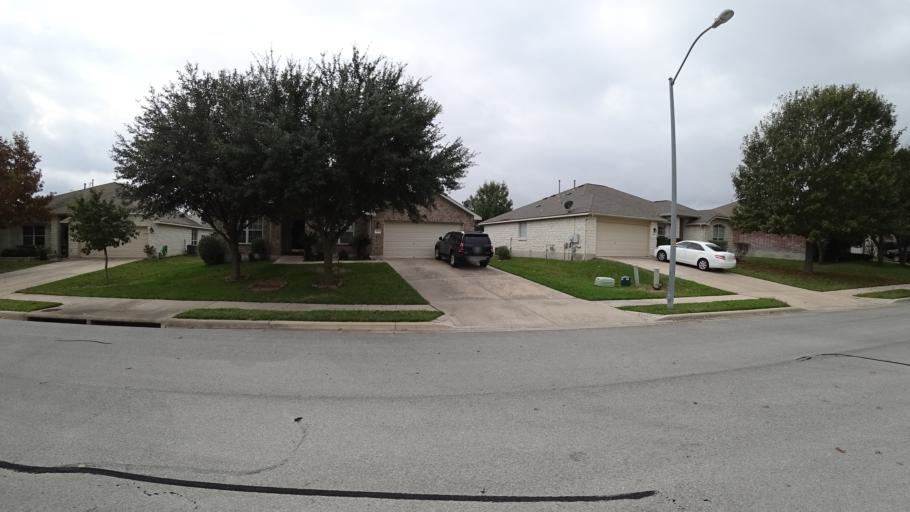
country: US
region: Texas
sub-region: Travis County
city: Pflugerville
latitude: 30.4406
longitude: -97.6026
